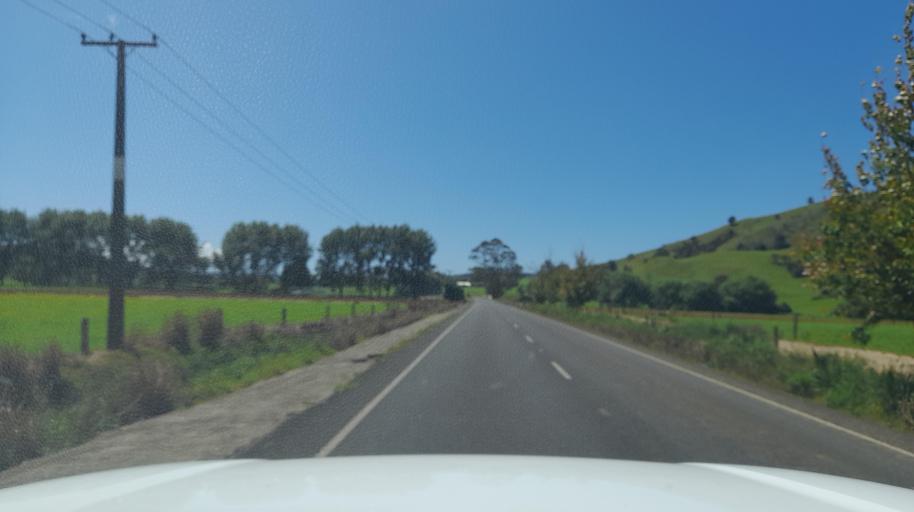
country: NZ
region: Northland
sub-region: Far North District
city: Taipa
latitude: -35.0638
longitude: 173.5024
